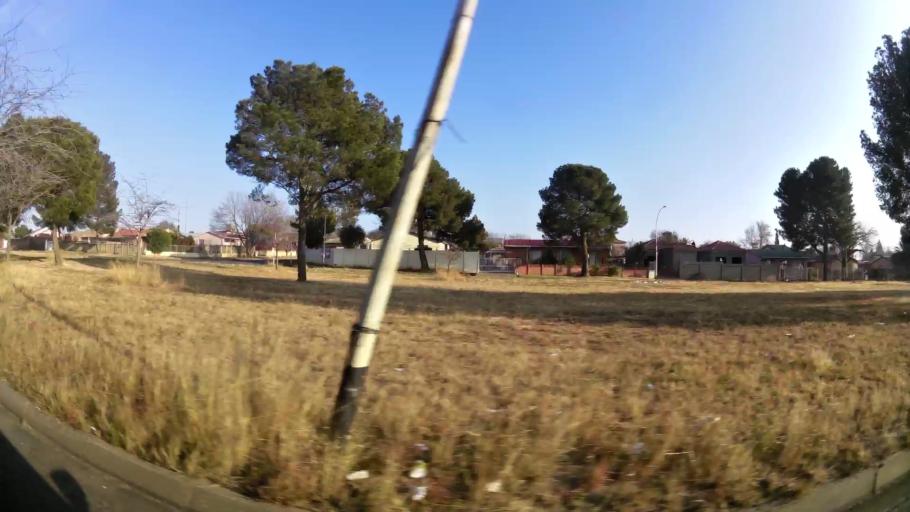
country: ZA
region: Orange Free State
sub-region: Mangaung Metropolitan Municipality
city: Bloemfontein
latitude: -29.1646
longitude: 26.2009
